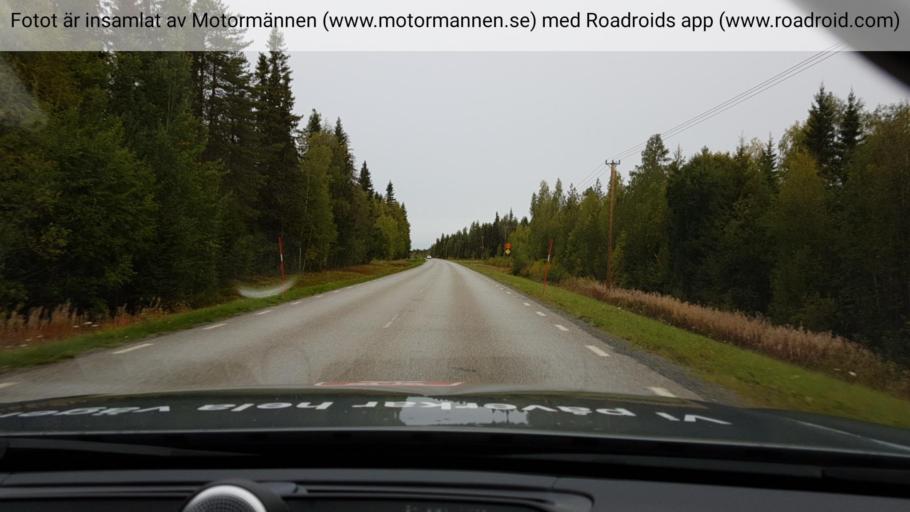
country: SE
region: Jaemtland
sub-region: Stroemsunds Kommun
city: Stroemsund
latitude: 63.9208
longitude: 15.5159
